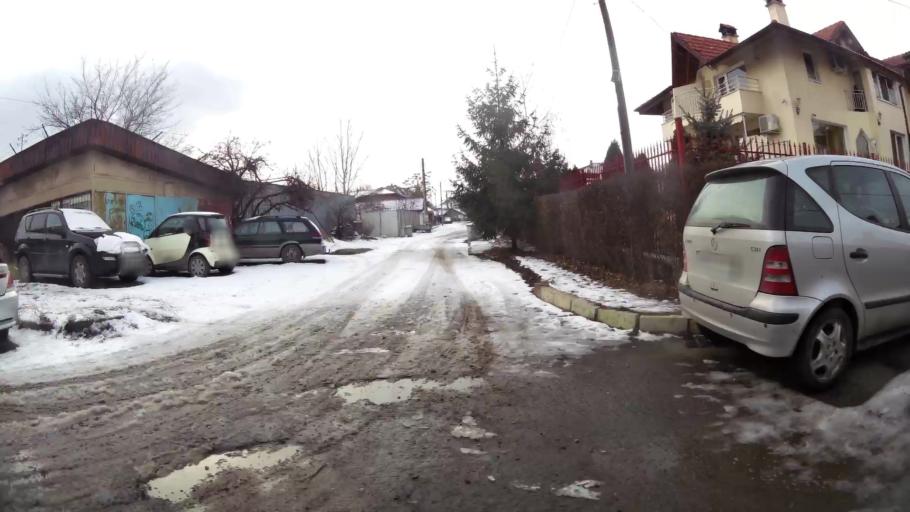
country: BG
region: Sofia-Capital
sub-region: Stolichna Obshtina
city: Sofia
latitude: 42.7018
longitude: 23.3843
